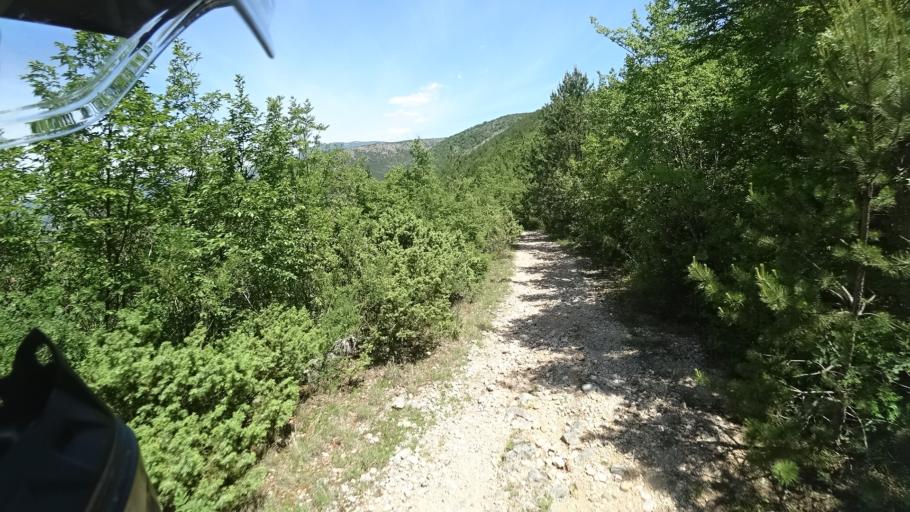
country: HR
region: Sibensko-Kniniska
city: Knin
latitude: 44.0333
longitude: 16.2283
